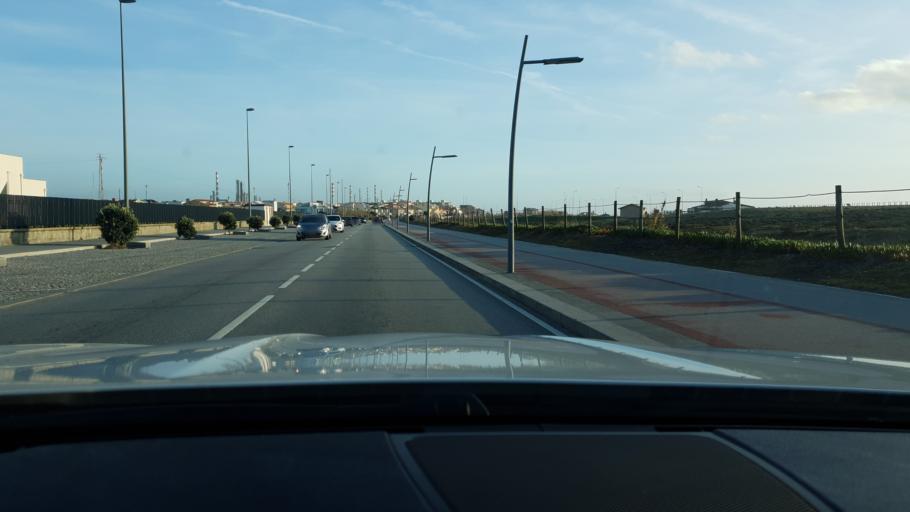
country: PT
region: Porto
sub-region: Matosinhos
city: Lavra
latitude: 41.2335
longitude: -8.7206
